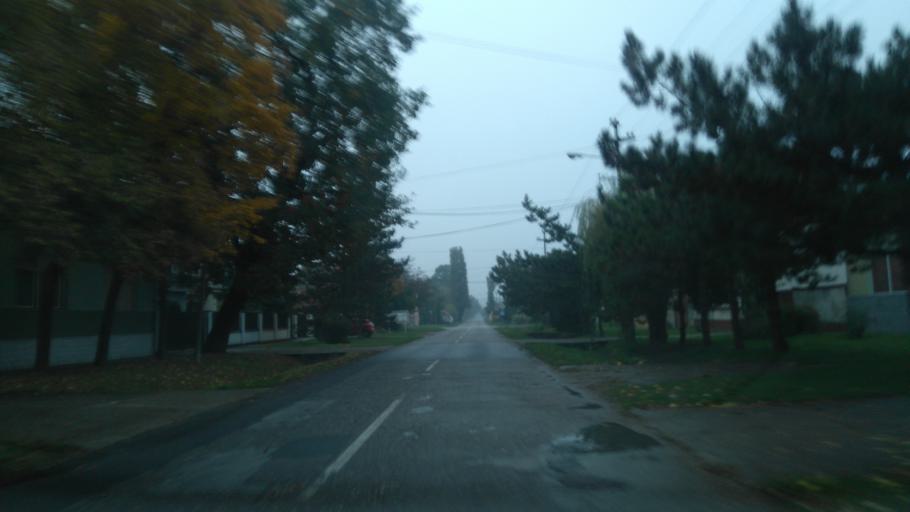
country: RS
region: Autonomna Pokrajina Vojvodina
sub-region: Juznobacki Okrug
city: Becej
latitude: 45.6158
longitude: 20.0392
